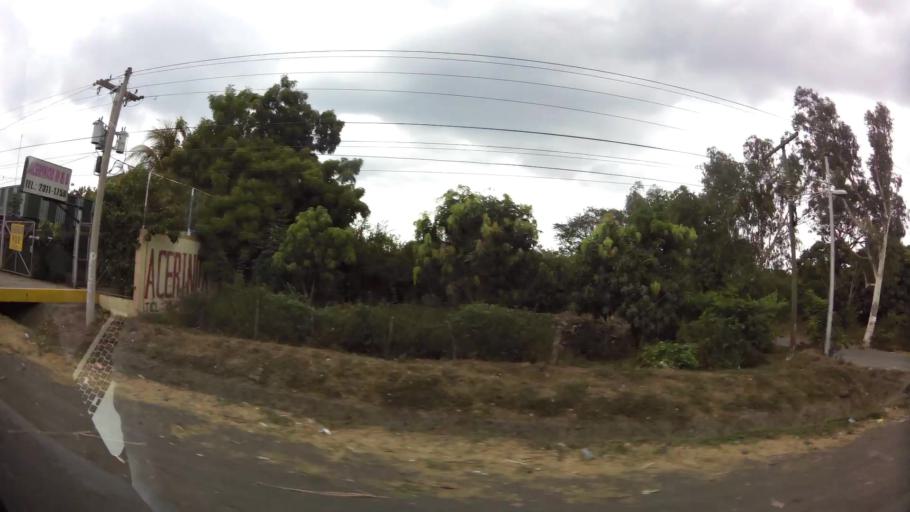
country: NI
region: Leon
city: Leon
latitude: 12.4657
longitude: -86.8658
